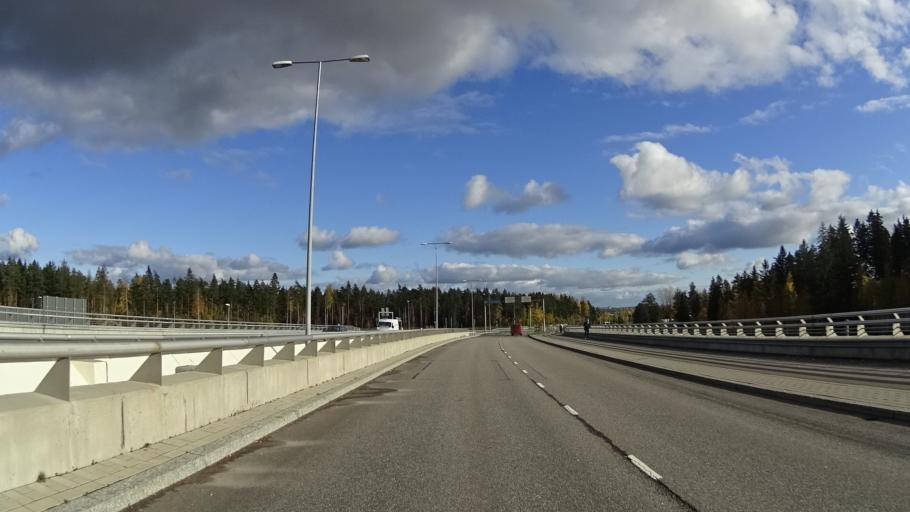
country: FI
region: Uusimaa
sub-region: Helsinki
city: Vantaa
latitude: 60.3017
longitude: 24.9602
